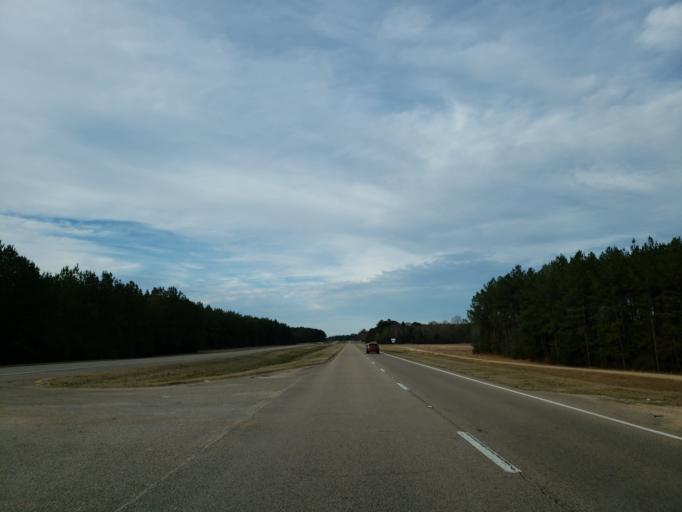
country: US
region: Mississippi
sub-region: Wayne County
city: Waynesboro
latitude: 31.6369
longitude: -88.5935
